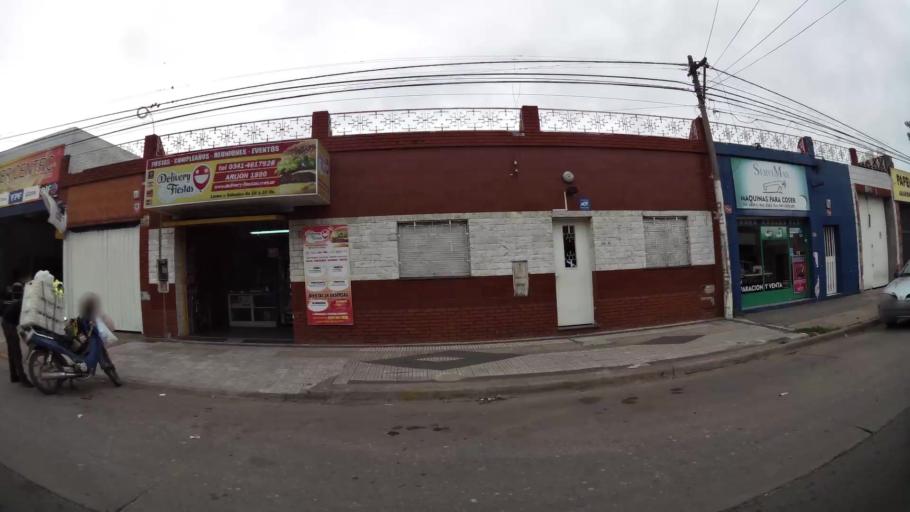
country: AR
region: Santa Fe
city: Gobernador Galvez
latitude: -33.0034
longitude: -60.6603
